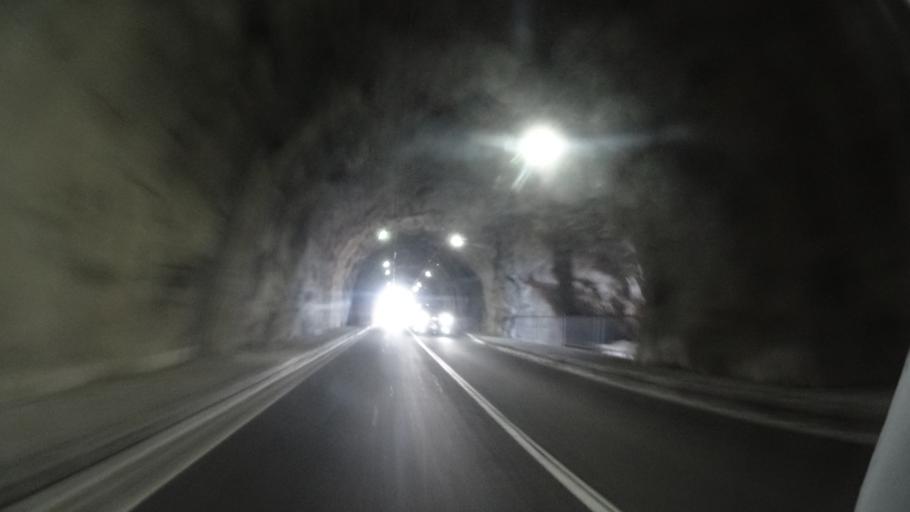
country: JP
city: Asahi
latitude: 35.9635
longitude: 135.9707
